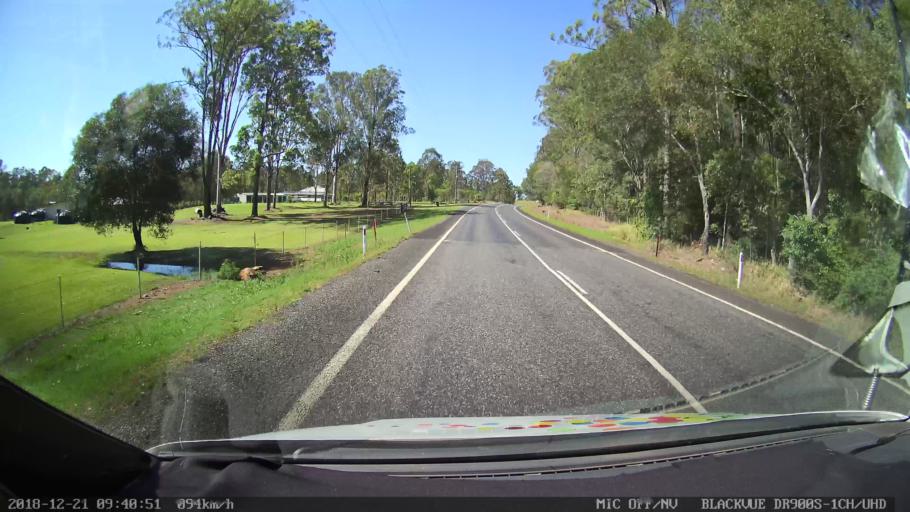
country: AU
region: New South Wales
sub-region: Clarence Valley
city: Grafton
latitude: -29.5783
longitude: 152.9621
